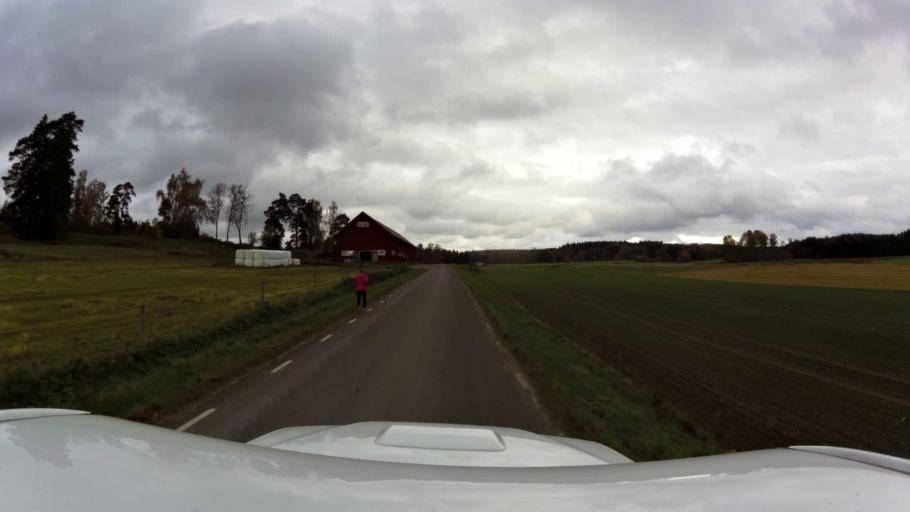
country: SE
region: OEstergoetland
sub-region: Motala Kommun
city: Borensberg
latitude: 58.5689
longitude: 15.3883
